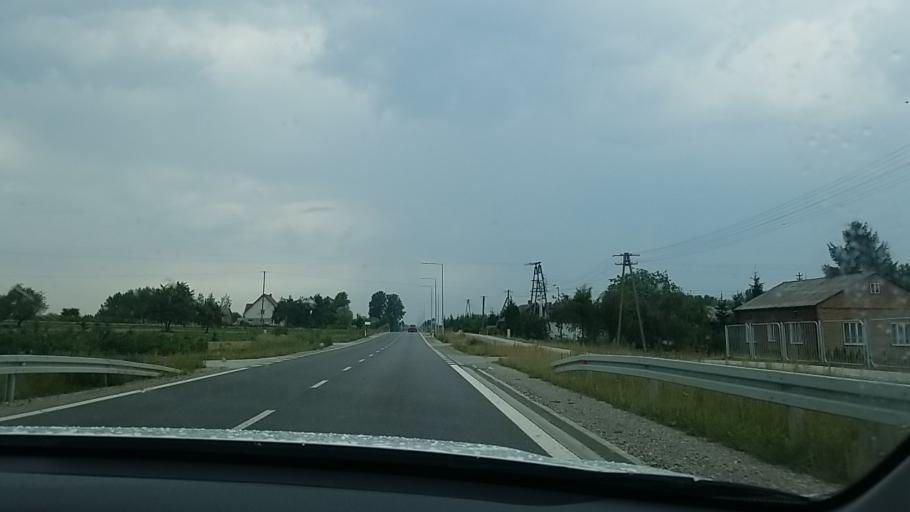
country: PL
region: Lublin Voivodeship
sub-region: Powiat lubelski
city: Jablonna
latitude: 51.0437
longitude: 22.6382
